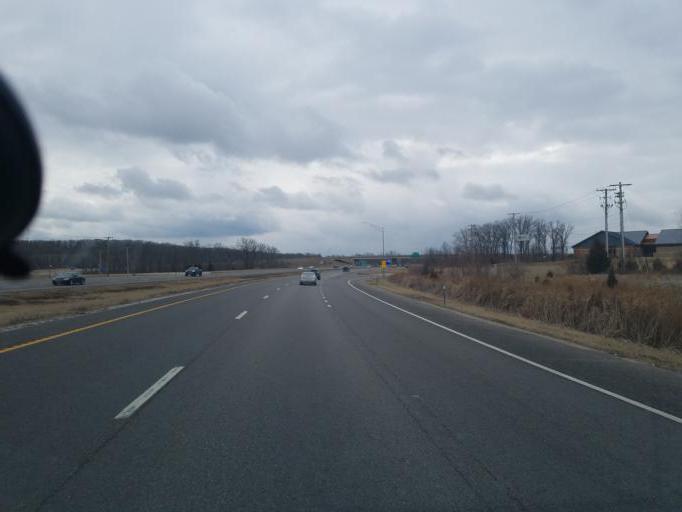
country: US
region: Missouri
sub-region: Boone County
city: Columbia
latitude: 38.9802
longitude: -92.2813
